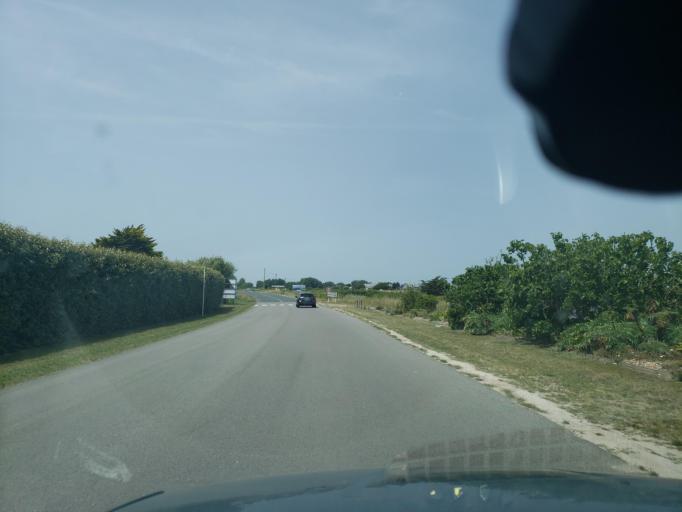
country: FR
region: Brittany
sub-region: Departement du Finistere
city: Guilvinec
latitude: 47.8023
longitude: -4.2984
